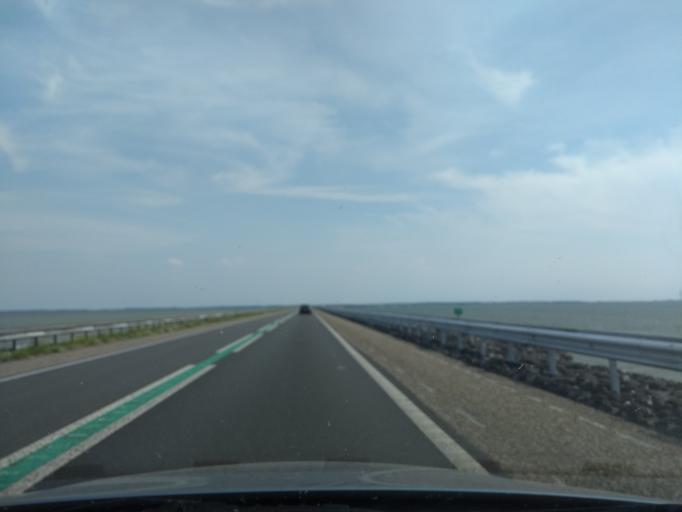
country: NL
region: Flevoland
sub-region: Gemeente Lelystad
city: Lelystad
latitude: 52.6039
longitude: 5.4454
